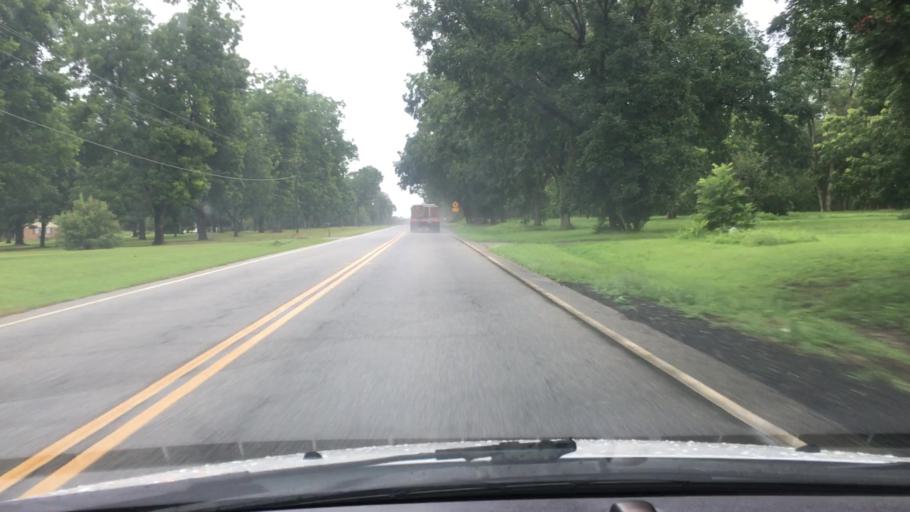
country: US
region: Georgia
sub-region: Grady County
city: Cairo
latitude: 30.7852
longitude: -84.2747
